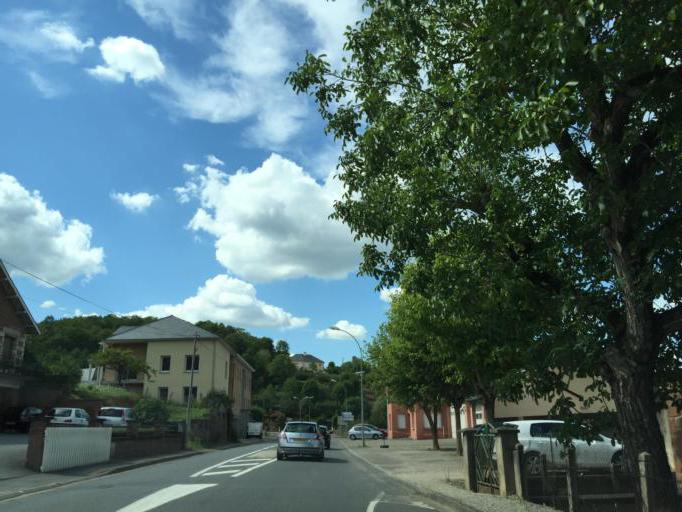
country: FR
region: Midi-Pyrenees
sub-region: Departement de l'Aveyron
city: Marcillac-Vallon
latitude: 44.4763
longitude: 2.4563
